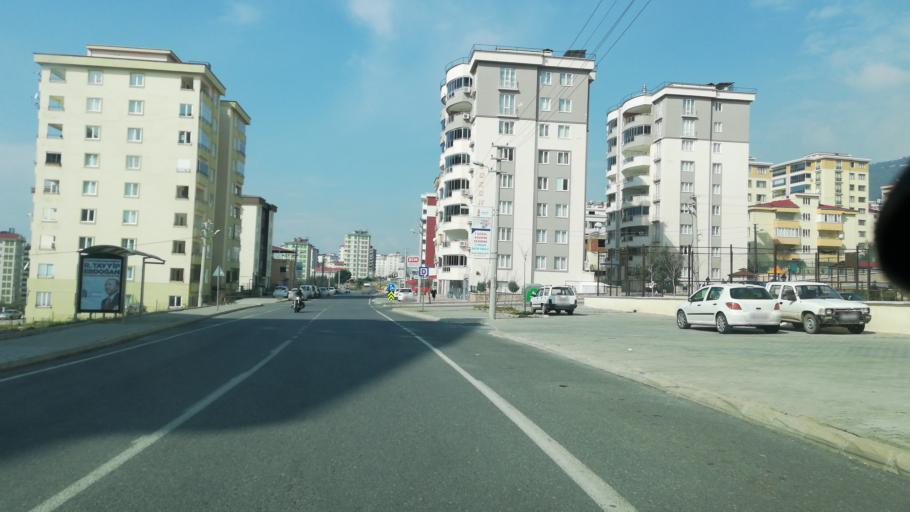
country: TR
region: Kahramanmaras
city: Kahramanmaras
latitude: 37.5880
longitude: 36.8656
